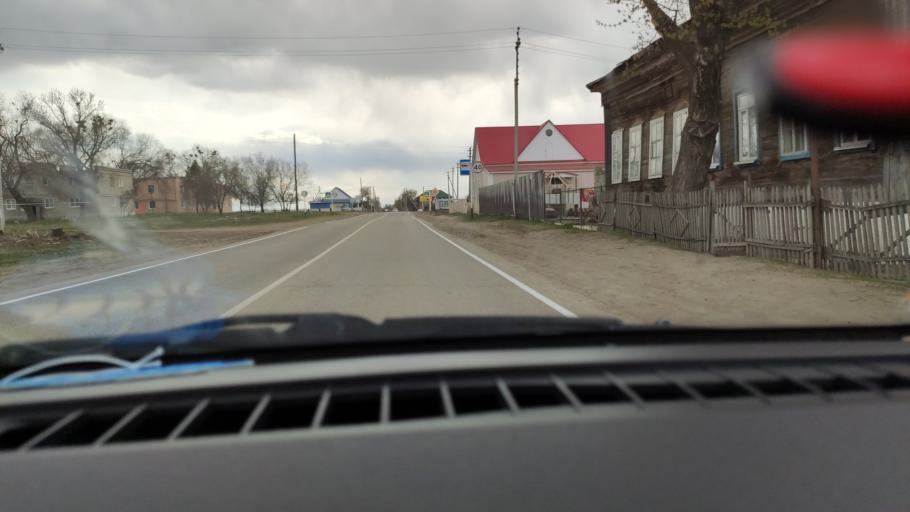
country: RU
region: Saratov
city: Privolzhskiy
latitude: 51.2021
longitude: 45.9167
